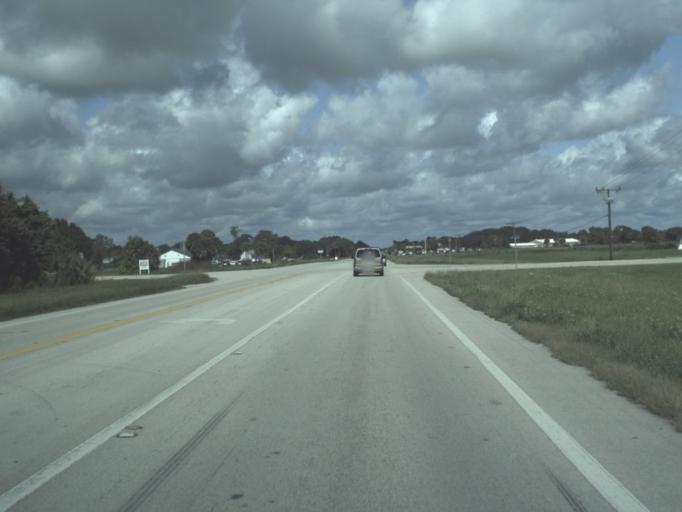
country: US
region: Florida
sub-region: Okeechobee County
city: Okeechobee
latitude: 27.2574
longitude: -80.8575
